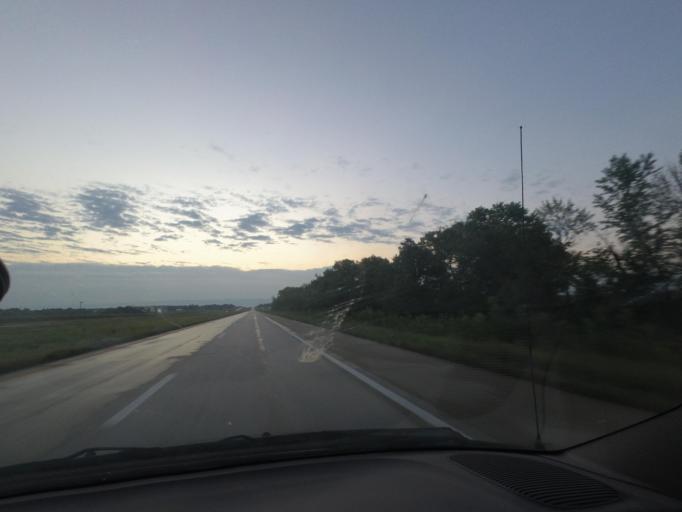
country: US
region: Missouri
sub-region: Macon County
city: Macon
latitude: 39.7598
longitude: -92.6831
